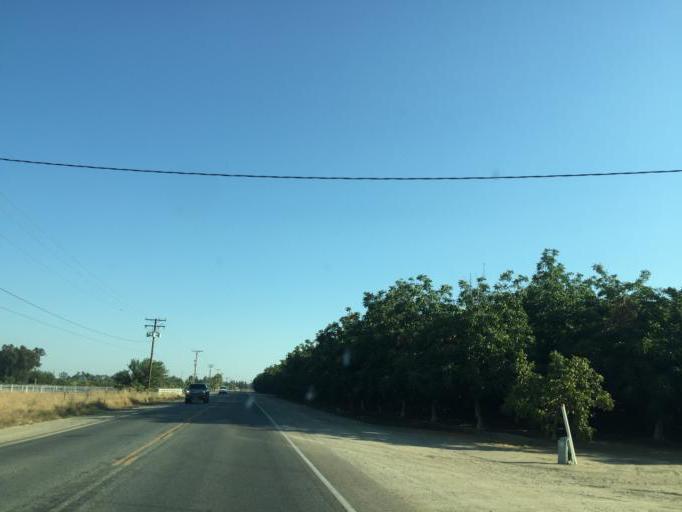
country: US
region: California
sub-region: Tulare County
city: Visalia
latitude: 36.3785
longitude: -119.2788
